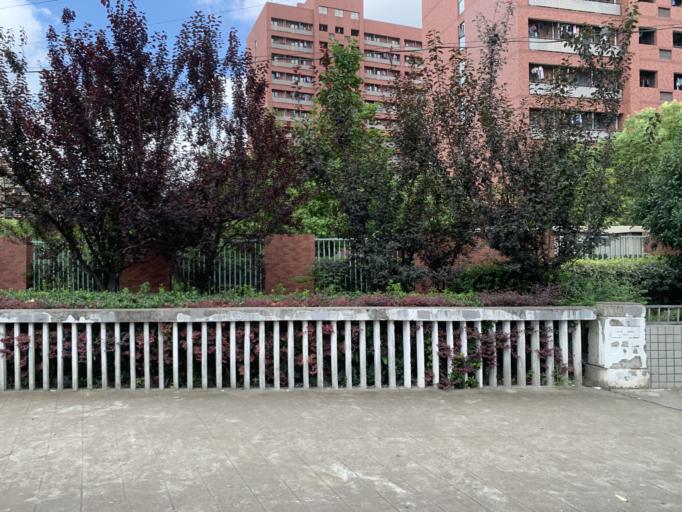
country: CN
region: Shanghai Shi
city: Huamu
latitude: 31.2030
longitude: 121.5297
